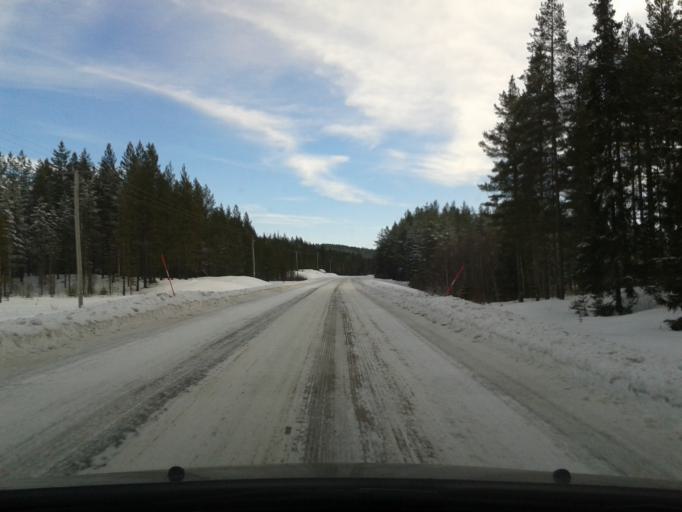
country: SE
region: Vaesterbotten
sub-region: Vilhelmina Kommun
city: Vilhelmina
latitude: 64.3845
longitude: 16.8897
